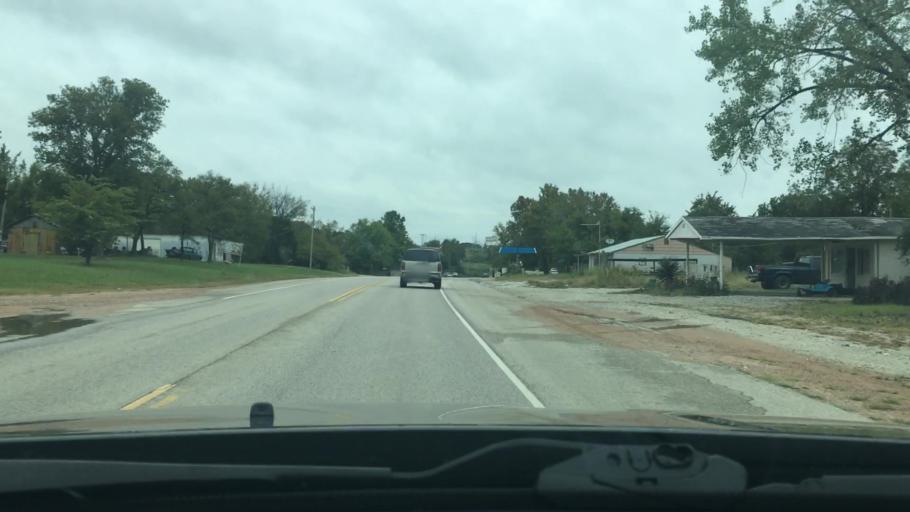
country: US
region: Oklahoma
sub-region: Pontotoc County
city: Ada
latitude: 34.6128
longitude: -96.6345
